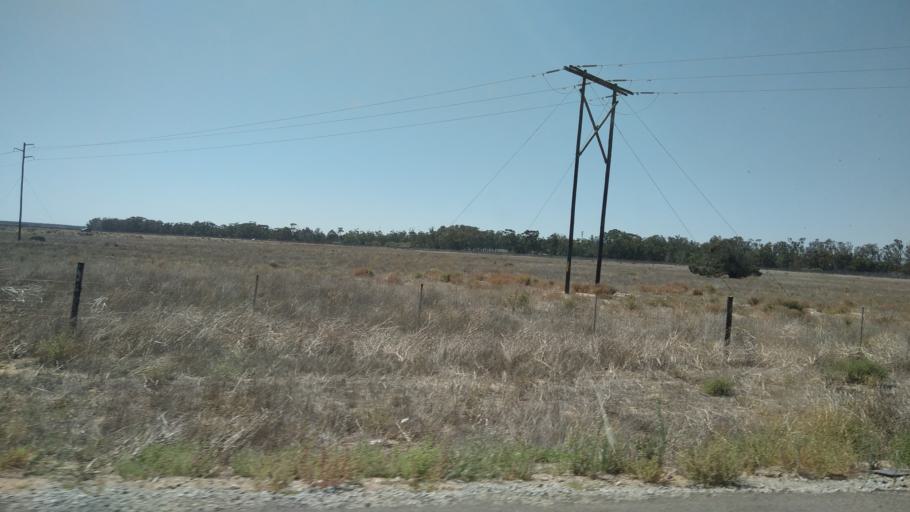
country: ZA
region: Western Cape
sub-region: West Coast District Municipality
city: Vredenburg
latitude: -32.9860
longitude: 18.1418
